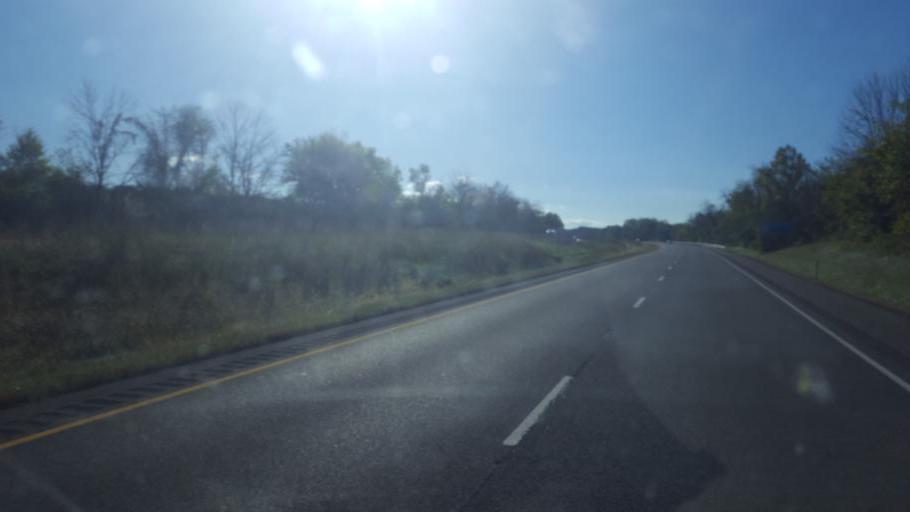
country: US
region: Maryland
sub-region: Washington County
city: Hancock
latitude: 39.6340
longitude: -78.0239
